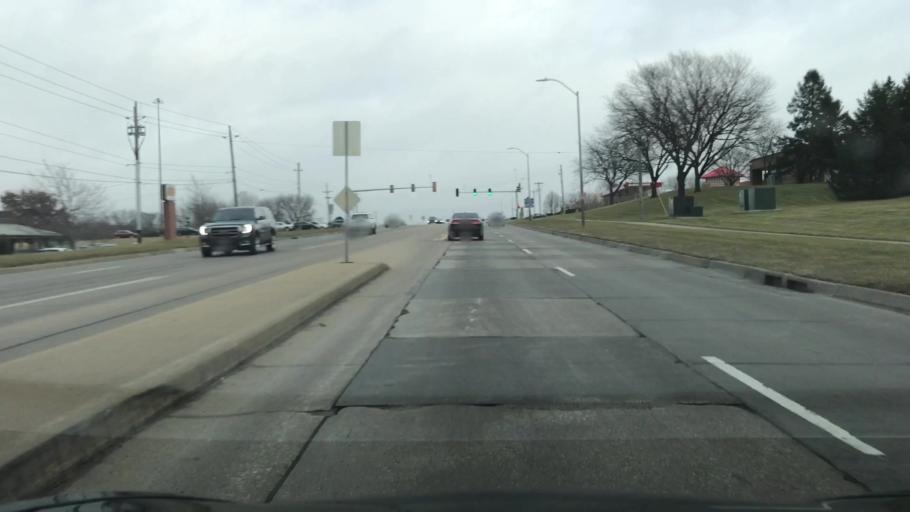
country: US
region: Iowa
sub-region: Polk County
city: Clive
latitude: 41.6004
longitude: -93.7813
